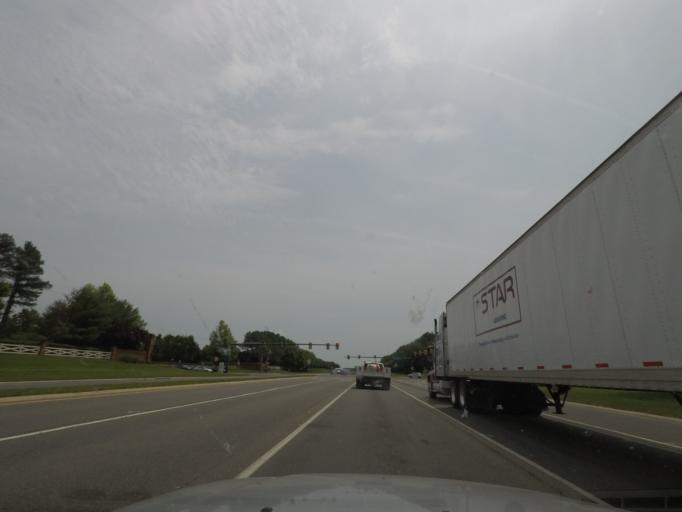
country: US
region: Virginia
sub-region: Prince William County
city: Haymarket
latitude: 38.8445
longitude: -77.6365
